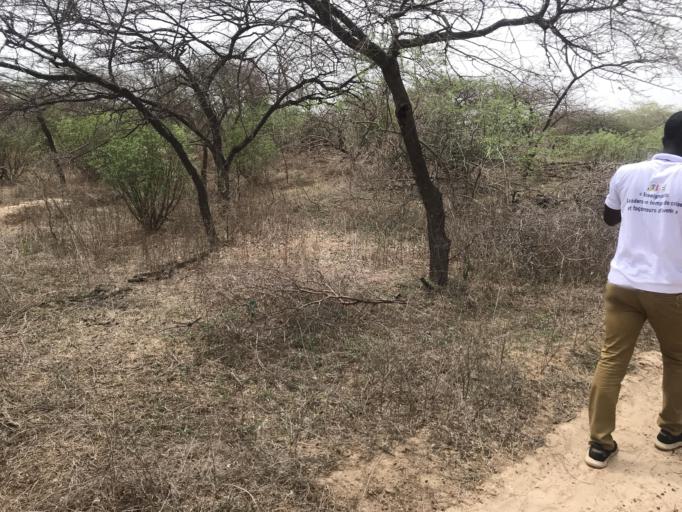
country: SN
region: Saint-Louis
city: Saint-Louis
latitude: 15.9089
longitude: -16.4572
